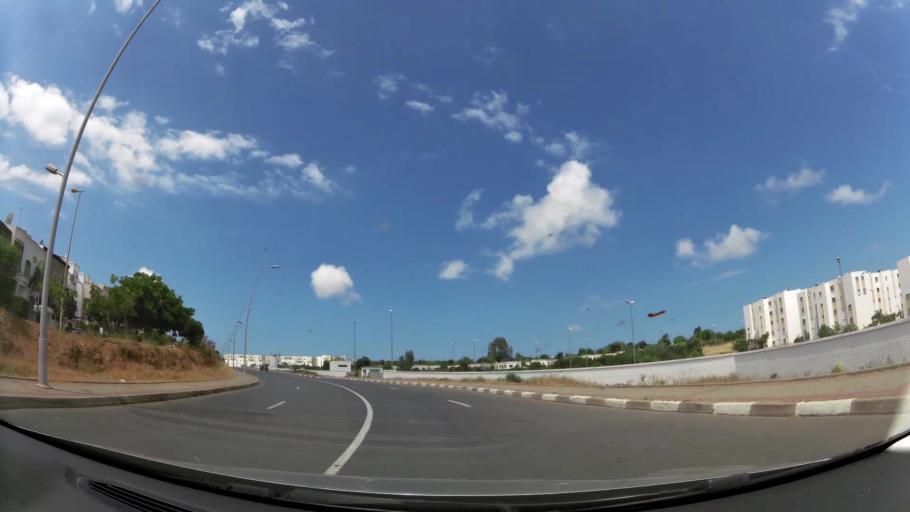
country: MA
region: Gharb-Chrarda-Beni Hssen
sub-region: Kenitra Province
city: Kenitra
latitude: 34.2775
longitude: -6.6064
